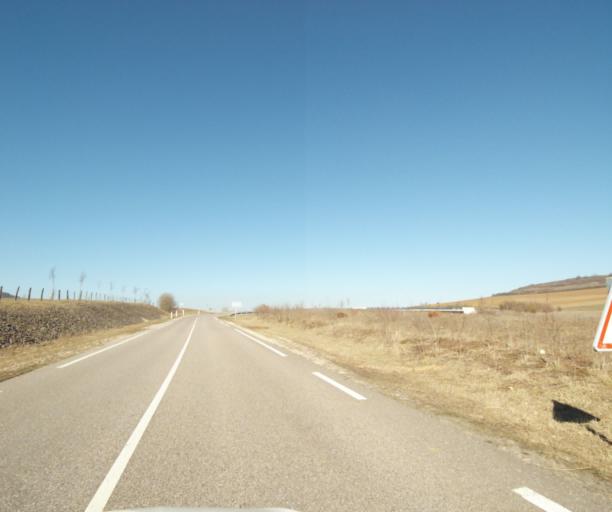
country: FR
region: Lorraine
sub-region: Departement de Meurthe-et-Moselle
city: Essey-les-Nancy
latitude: 48.7178
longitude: 6.2401
